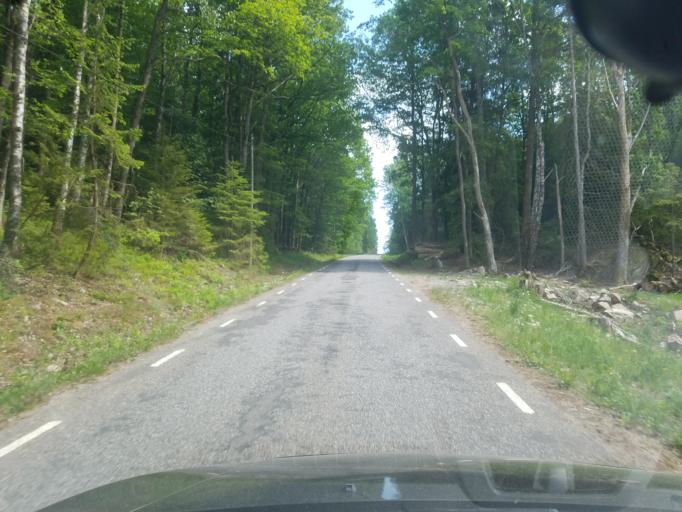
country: SE
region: Vaestra Goetaland
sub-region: Stenungsunds Kommun
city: Stora Hoga
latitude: 58.0036
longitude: 11.9219
